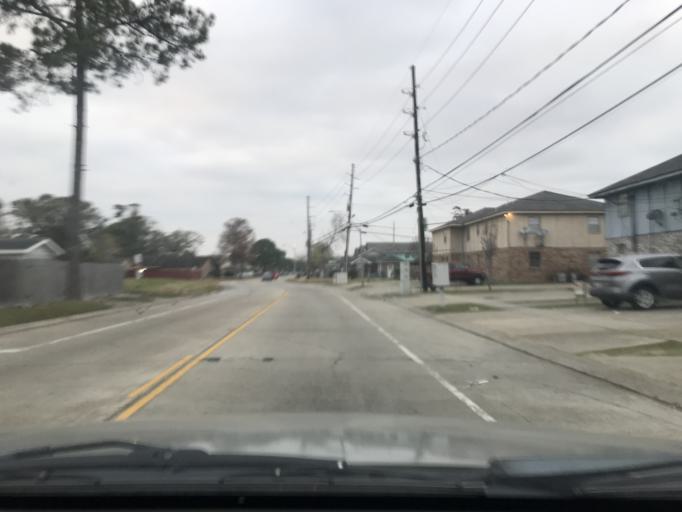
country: US
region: Louisiana
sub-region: Jefferson Parish
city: Woodmere
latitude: 29.8631
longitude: -90.0755
